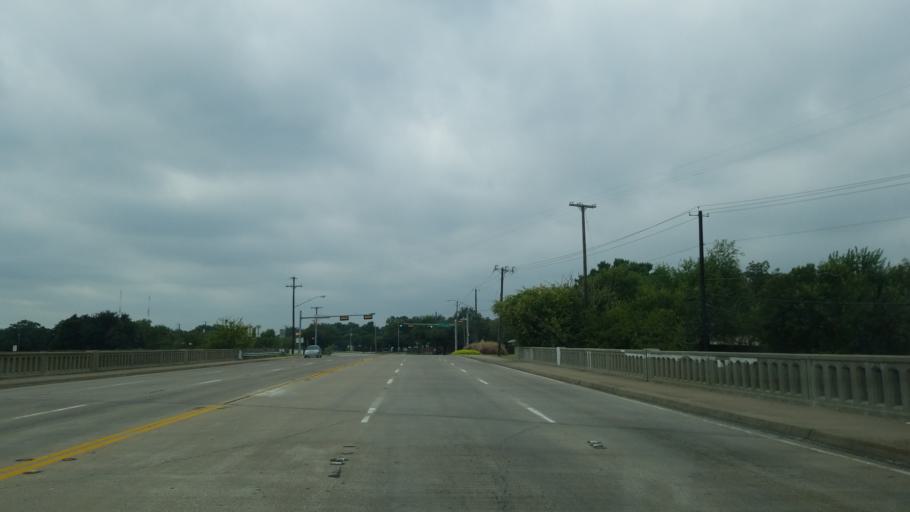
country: US
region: Texas
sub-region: Dallas County
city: Garland
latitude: 32.9079
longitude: -96.6483
